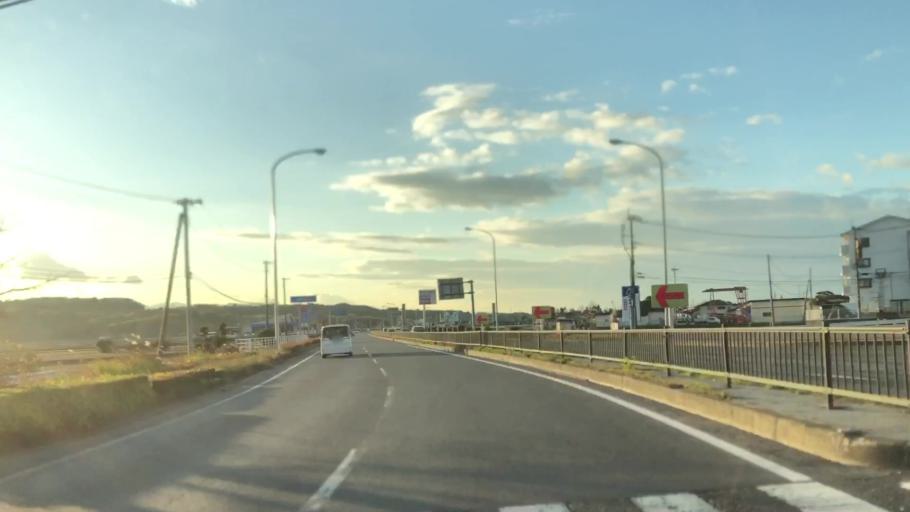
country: JP
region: Fukuoka
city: Nakatsu
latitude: 33.5511
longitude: 131.2736
